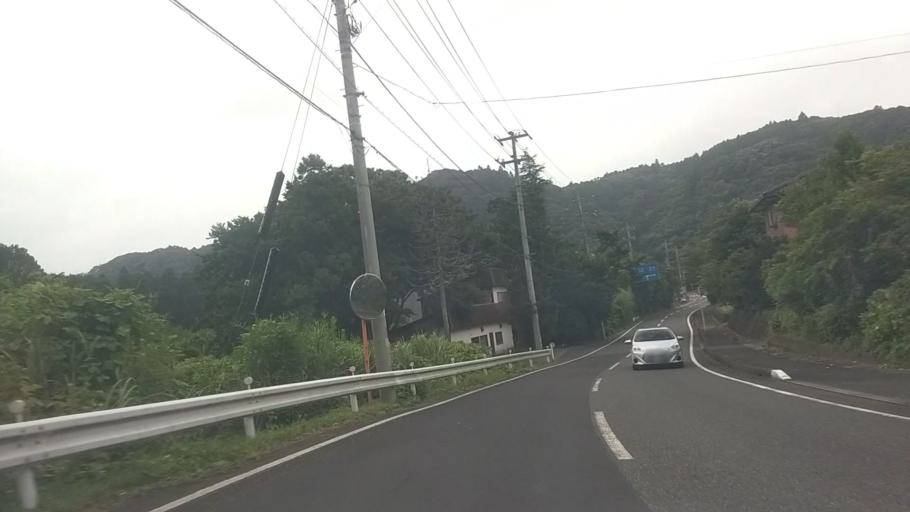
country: JP
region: Chiba
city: Ohara
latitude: 35.2687
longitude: 140.2540
